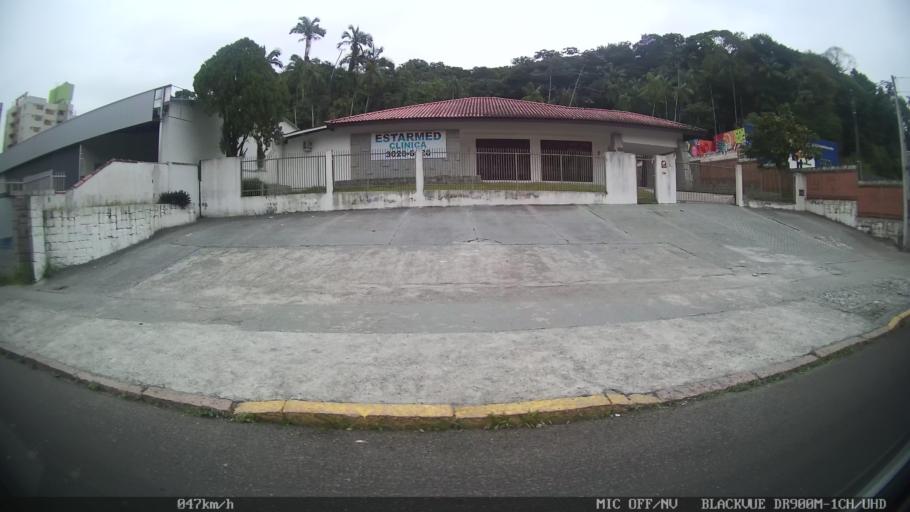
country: BR
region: Santa Catarina
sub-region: Joinville
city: Joinville
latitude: -26.3187
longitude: -48.8566
